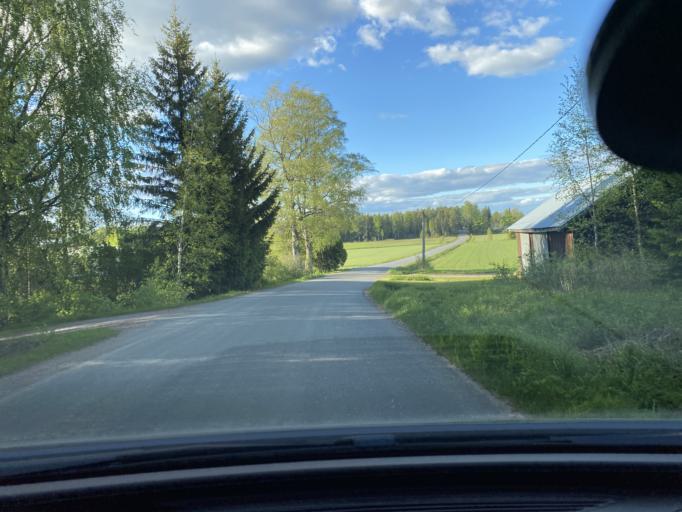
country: FI
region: Satakunta
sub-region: Pori
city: Huittinen
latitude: 61.1273
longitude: 22.8115
